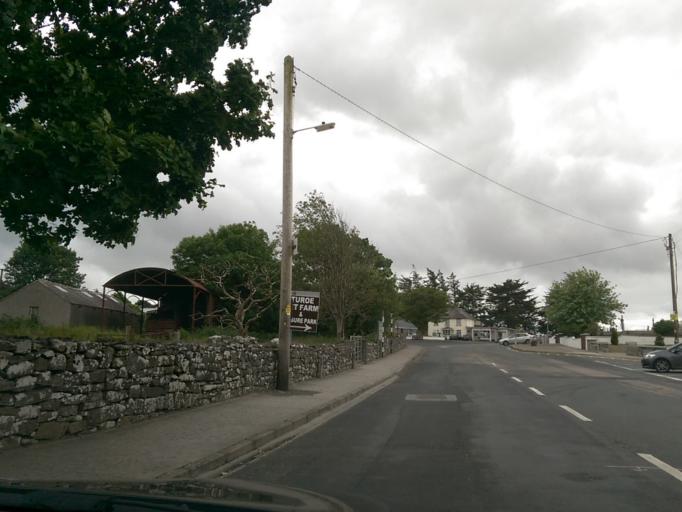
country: IE
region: Connaught
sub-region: County Galway
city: Loughrea
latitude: 53.2487
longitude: -8.5546
